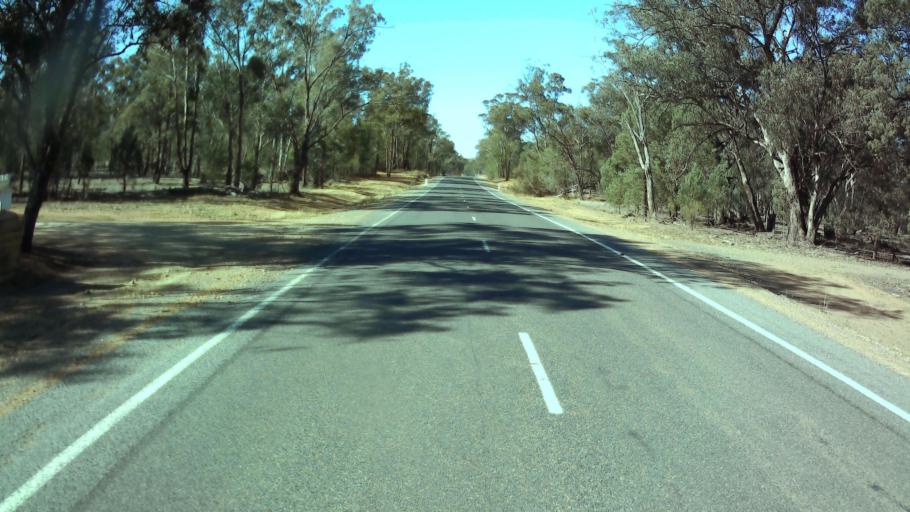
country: AU
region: New South Wales
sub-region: Weddin
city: Grenfell
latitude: -33.7516
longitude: 148.0845
